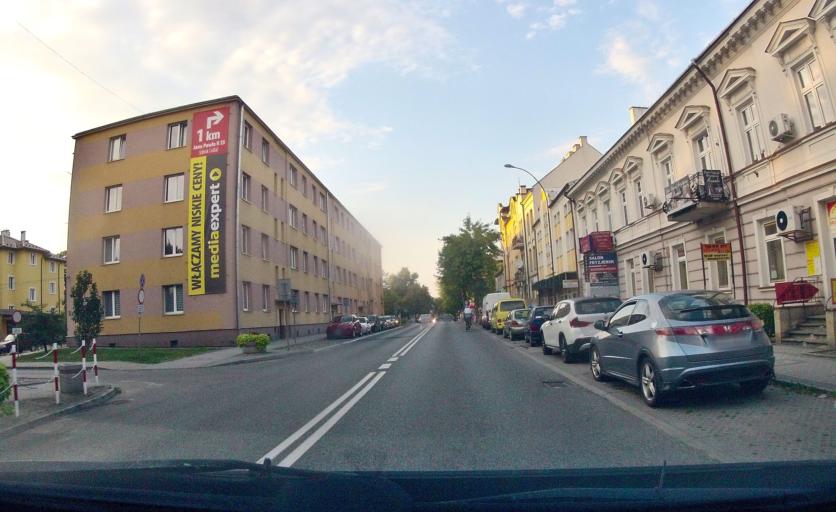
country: PL
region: Subcarpathian Voivodeship
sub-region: Powiat jasielski
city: Jaslo
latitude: 49.7429
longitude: 21.4734
